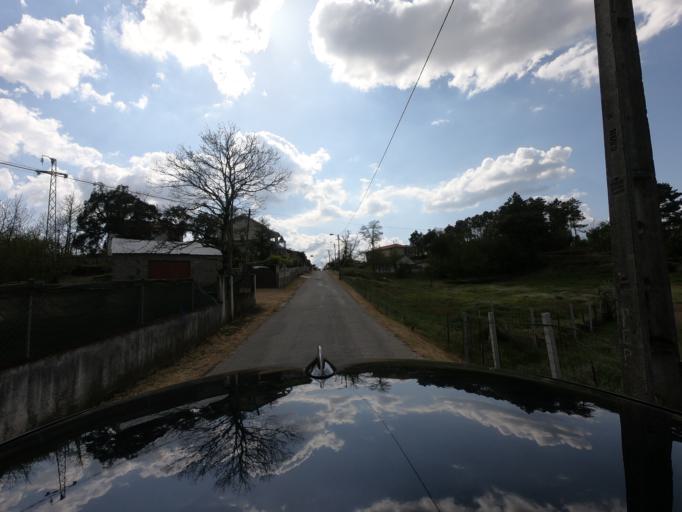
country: PT
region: Vila Real
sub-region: Sabrosa
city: Vilela
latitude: 41.2378
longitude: -7.6781
